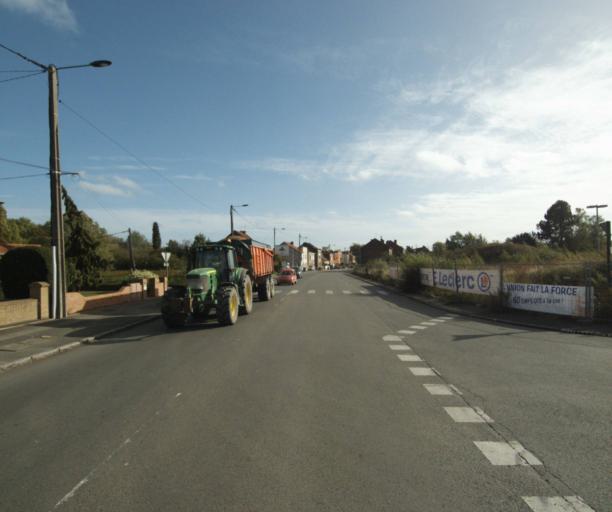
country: FR
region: Nord-Pas-de-Calais
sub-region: Departement du Nord
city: La Bassee
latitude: 50.5414
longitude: 2.8001
